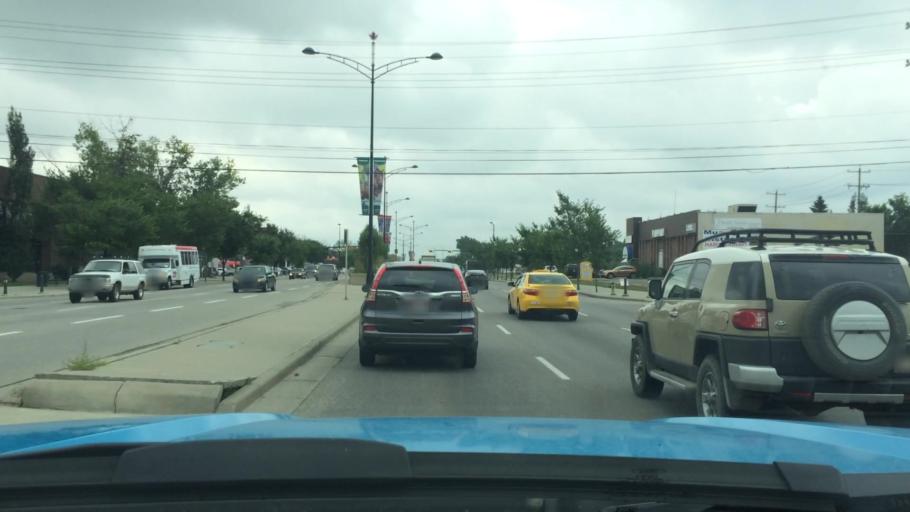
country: CA
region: Alberta
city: Calgary
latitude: 51.0669
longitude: -114.0538
